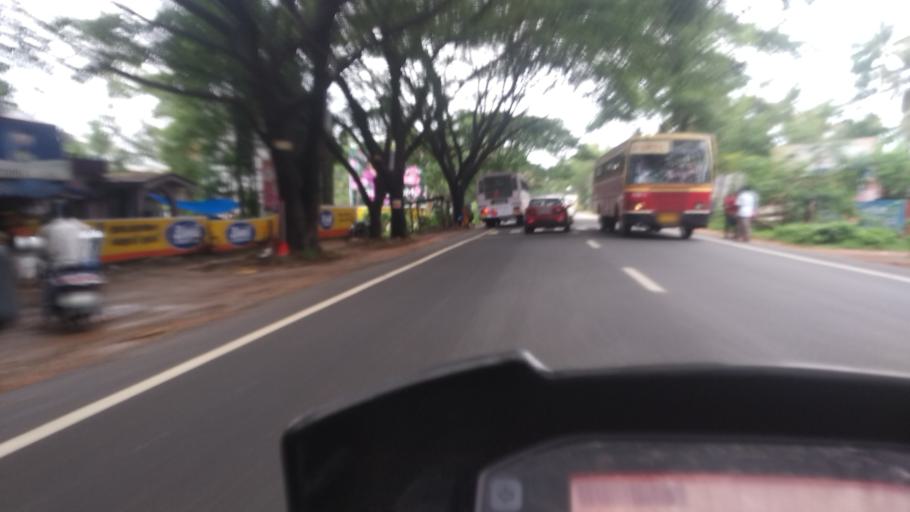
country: IN
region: Kerala
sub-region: Alappuzha
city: Alleppey
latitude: 9.5607
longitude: 76.3279
